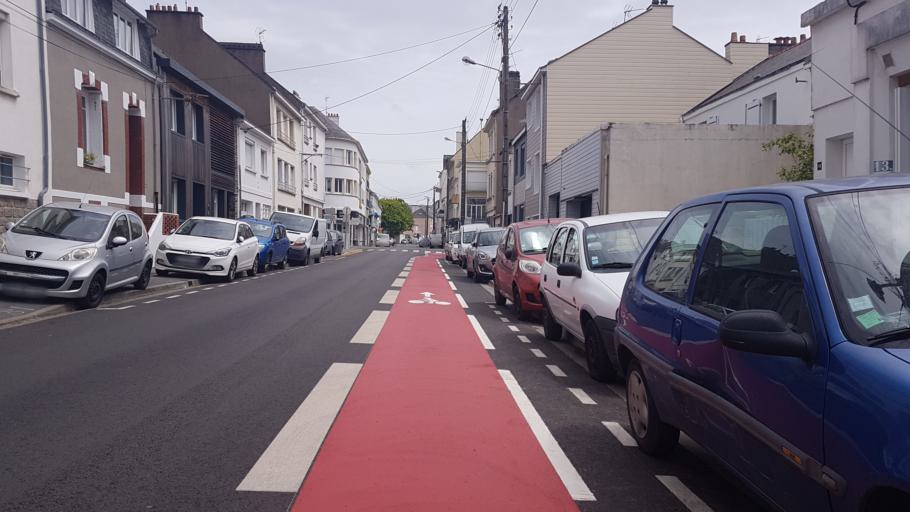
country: FR
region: Pays de la Loire
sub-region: Departement de la Loire-Atlantique
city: Saint-Nazaire
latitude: 47.2779
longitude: -2.2181
